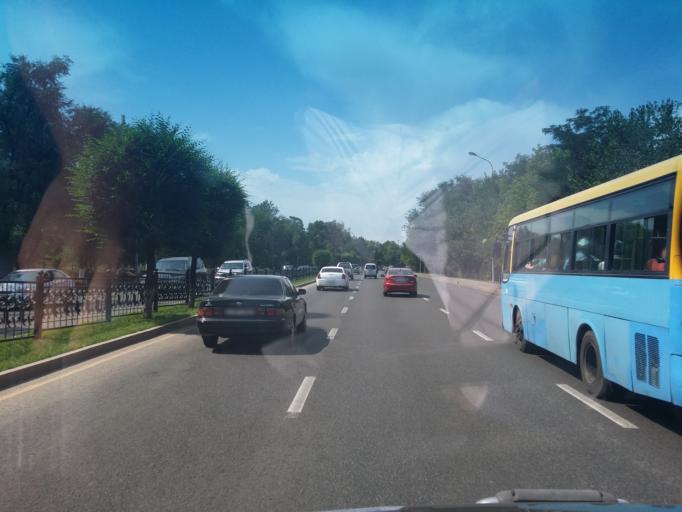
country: KZ
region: Almaty Qalasy
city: Almaty
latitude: 43.2034
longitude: 76.9126
